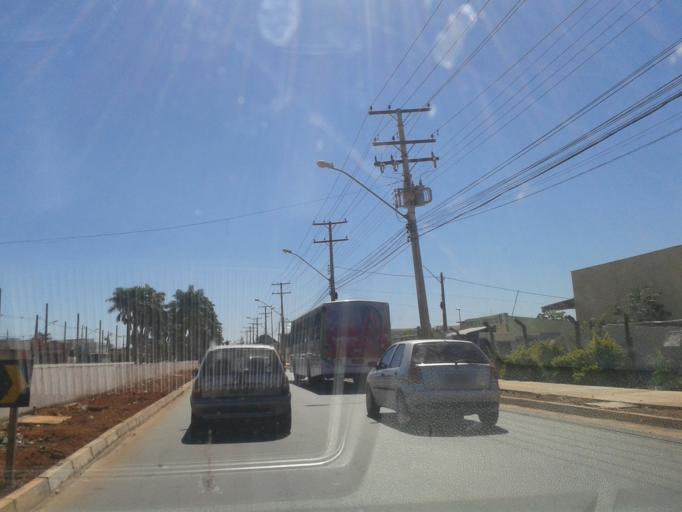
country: BR
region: Goias
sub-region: Goiania
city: Goiania
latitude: -16.6511
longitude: -49.2640
